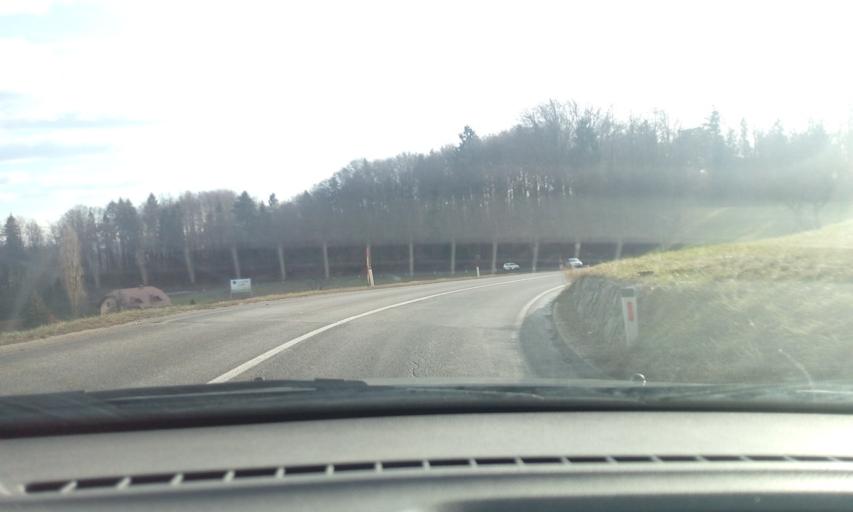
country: SI
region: Smarje pri Jelsah
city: Smarje pri Jelsah
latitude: 46.2305
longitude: 15.4846
